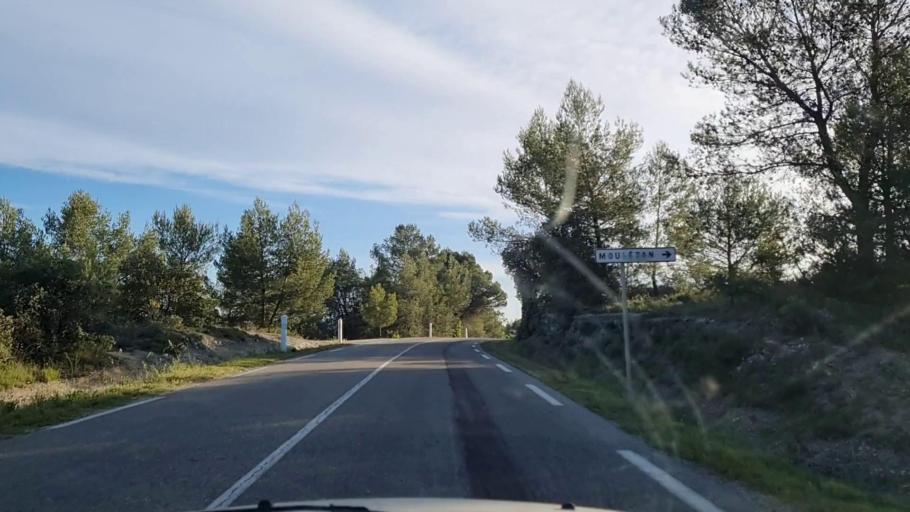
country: FR
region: Languedoc-Roussillon
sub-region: Departement du Gard
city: Ledignan
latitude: 43.9118
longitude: 4.1091
